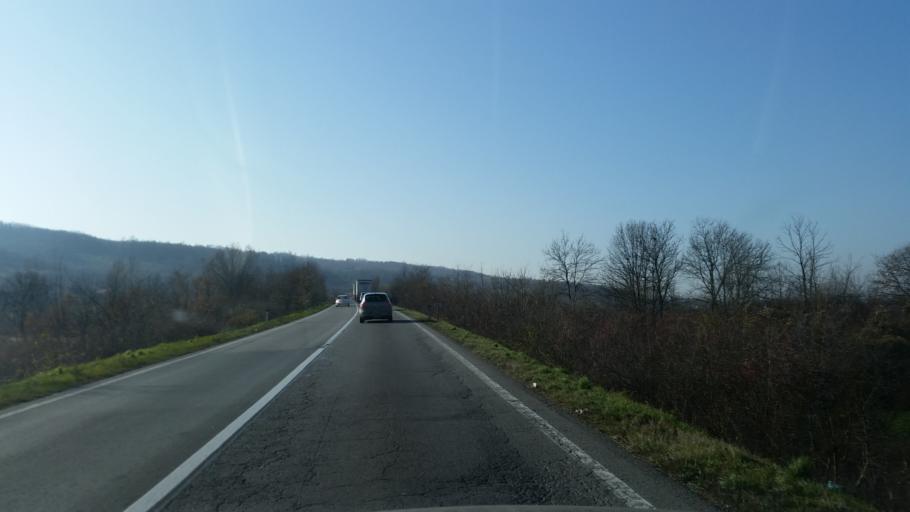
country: RS
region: Central Serbia
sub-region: Belgrade
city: Lazarevac
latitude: 44.3737
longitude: 20.2179
